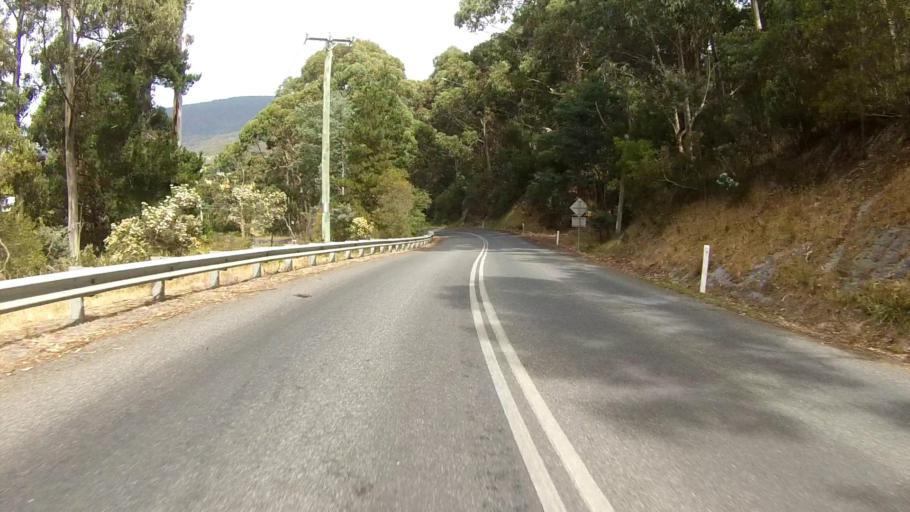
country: AU
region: Tasmania
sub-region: Kingborough
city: Kettering
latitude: -43.1476
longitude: 147.2408
